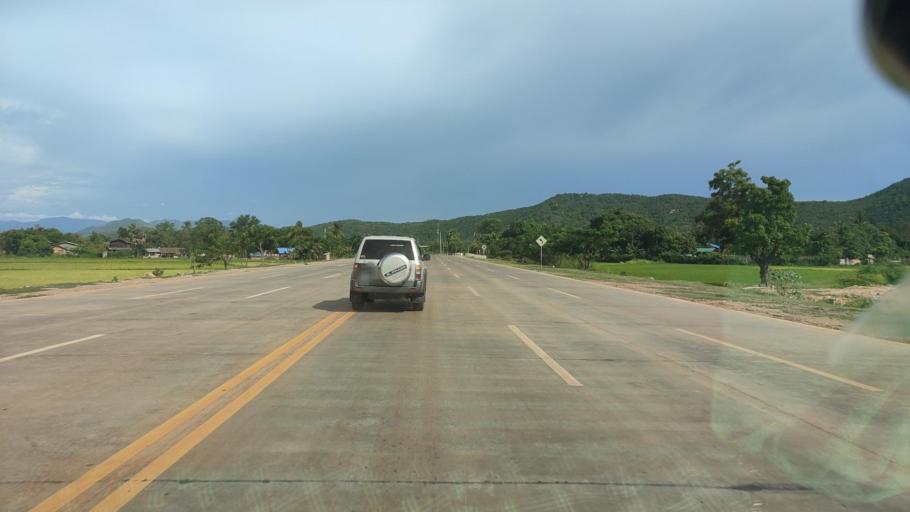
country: MM
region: Mandalay
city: Kyaukse
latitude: 21.6174
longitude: 96.1429
